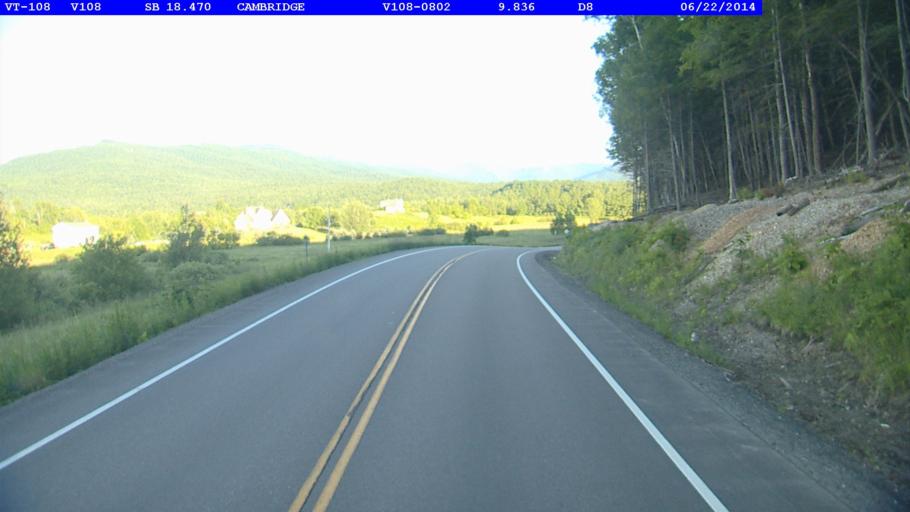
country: US
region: Vermont
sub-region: Lamoille County
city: Johnson
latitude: 44.6577
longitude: -72.8290
